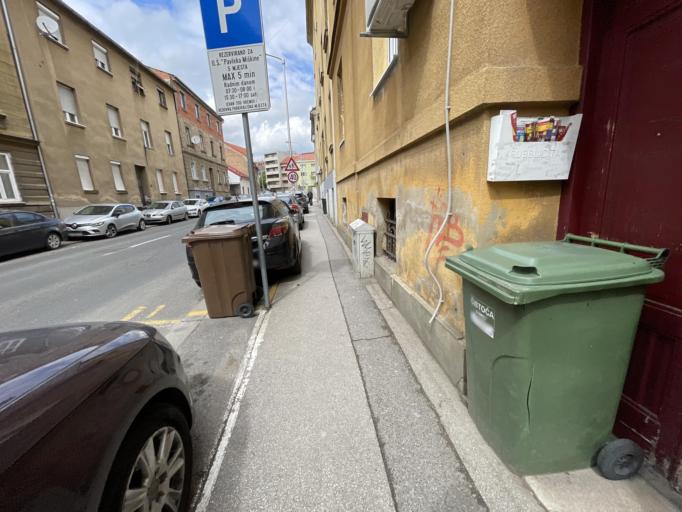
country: HR
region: Grad Zagreb
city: Zagreb - Centar
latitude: 45.8145
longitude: 15.9423
